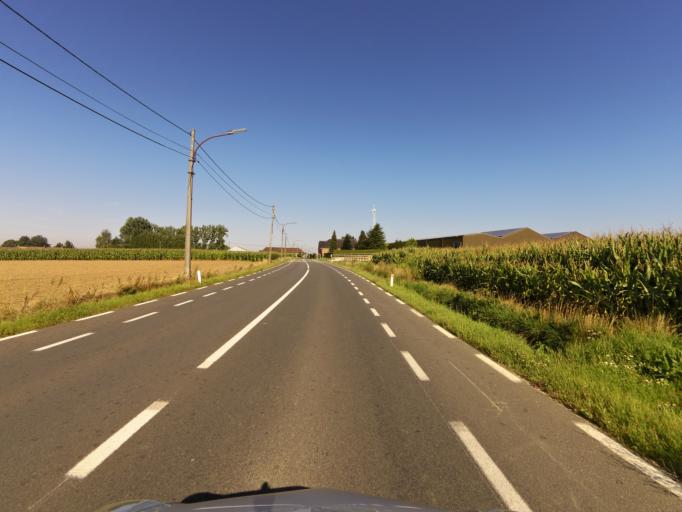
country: BE
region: Flanders
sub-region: Provincie Oost-Vlaanderen
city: Oudenaarde
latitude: 50.8232
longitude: 3.6915
